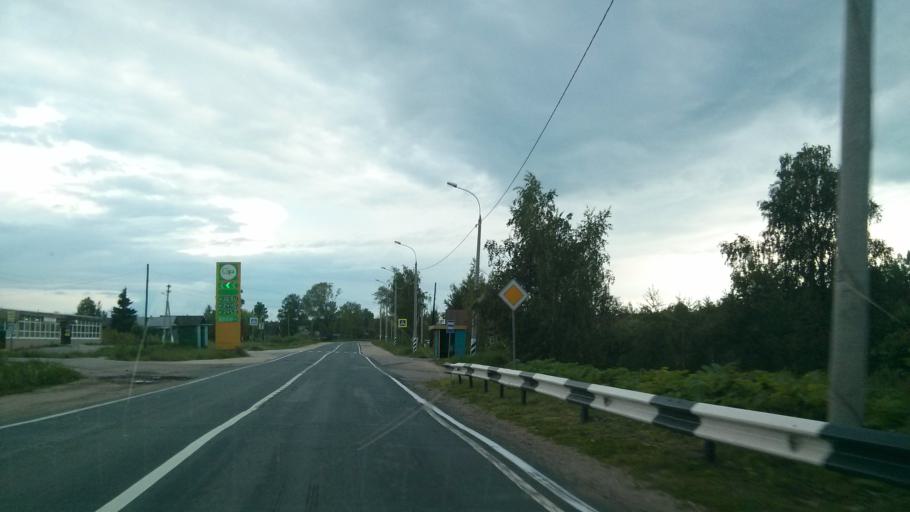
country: RU
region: Nizjnij Novgorod
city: Vacha
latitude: 55.7553
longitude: 42.5185
